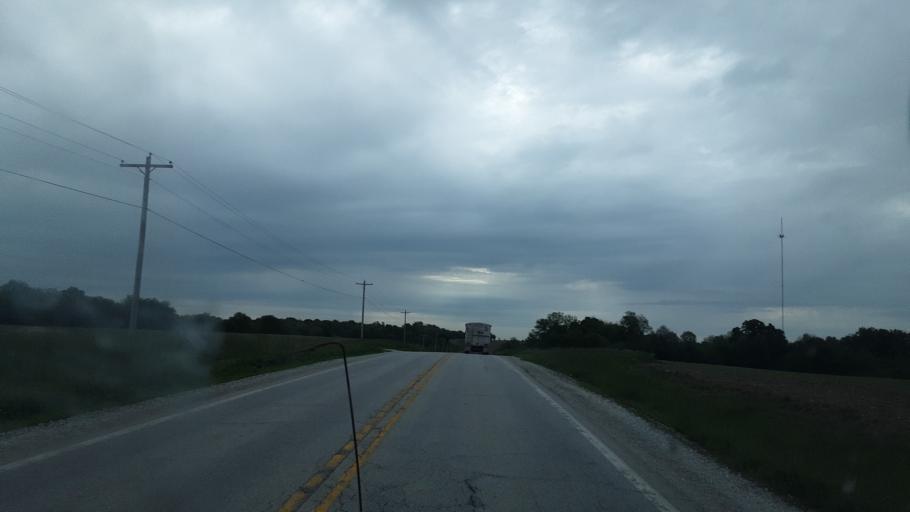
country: US
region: Illinois
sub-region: Fulton County
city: Lewistown
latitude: 40.3421
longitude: -90.2191
